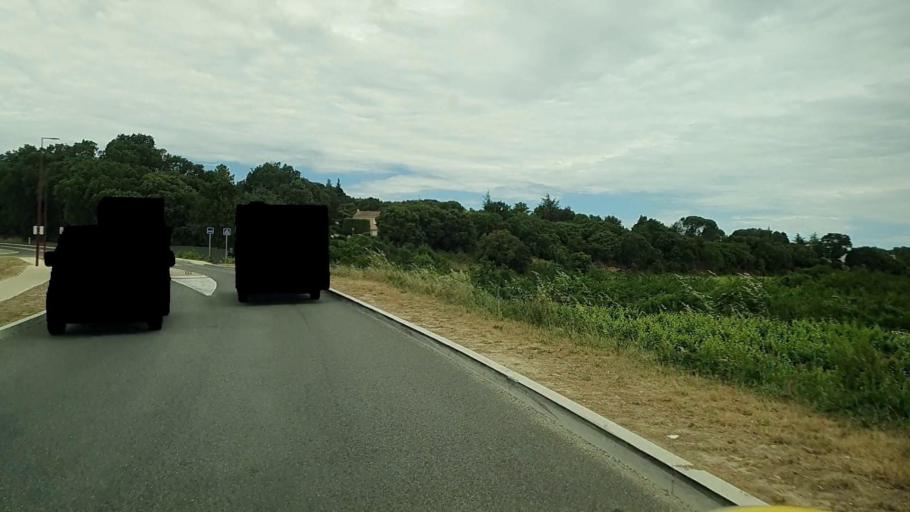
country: FR
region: Languedoc-Roussillon
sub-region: Departement du Gard
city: Connaux
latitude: 44.0449
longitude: 4.5787
